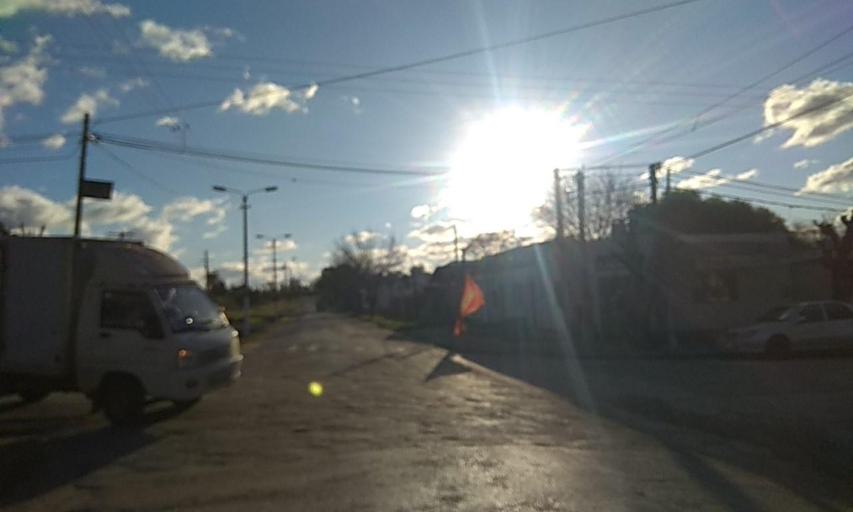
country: UY
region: Florida
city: Florida
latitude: -34.1013
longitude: -56.2281
